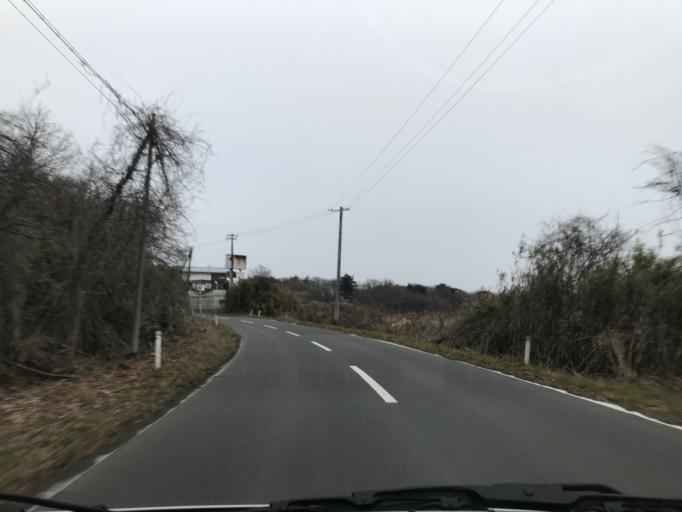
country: JP
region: Miyagi
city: Wakuya
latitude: 38.6748
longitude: 141.1048
